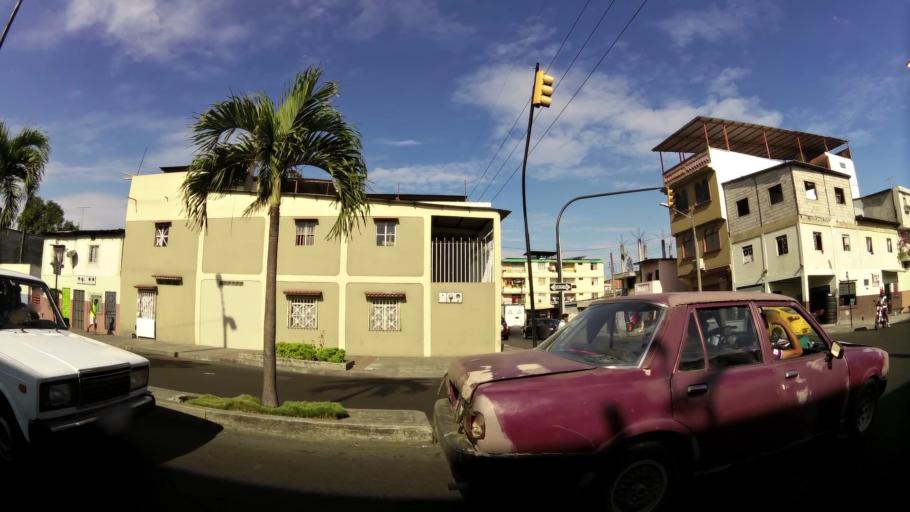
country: EC
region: Guayas
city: Guayaquil
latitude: -2.1942
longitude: -79.9135
